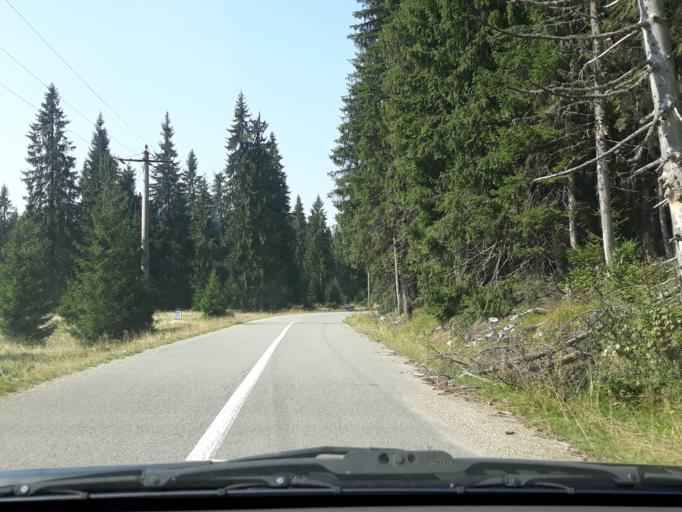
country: RO
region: Alba
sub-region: Comuna Arieseni
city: Arieseni
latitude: 46.5962
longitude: 22.7066
